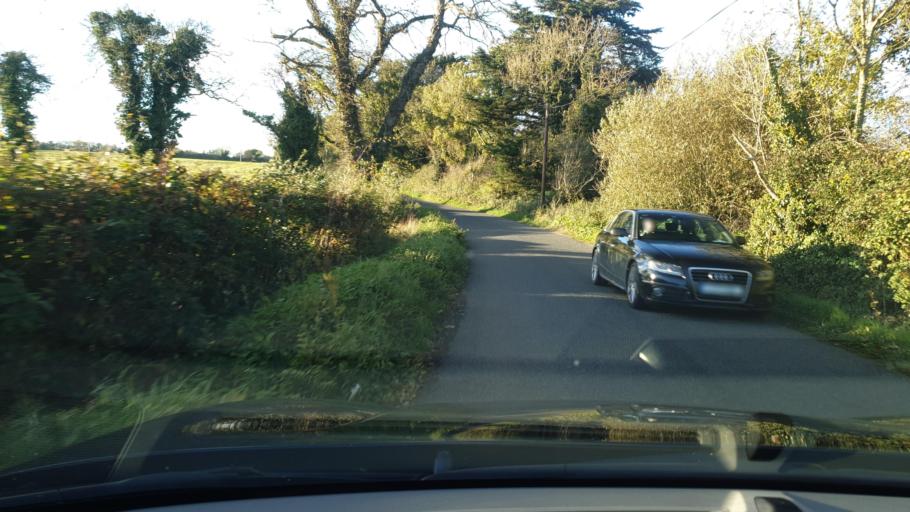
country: IE
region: Leinster
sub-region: An Mhi
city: Stamullin
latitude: 53.6353
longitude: -6.2850
